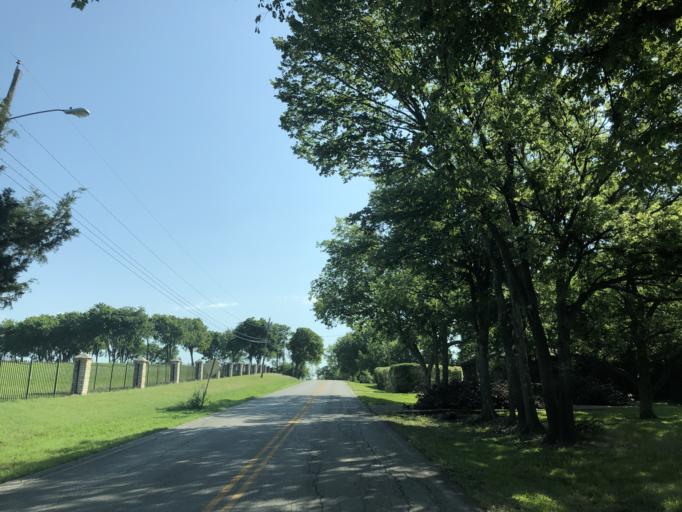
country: US
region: Texas
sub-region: Dallas County
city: Sunnyvale
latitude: 32.8303
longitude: -96.5641
